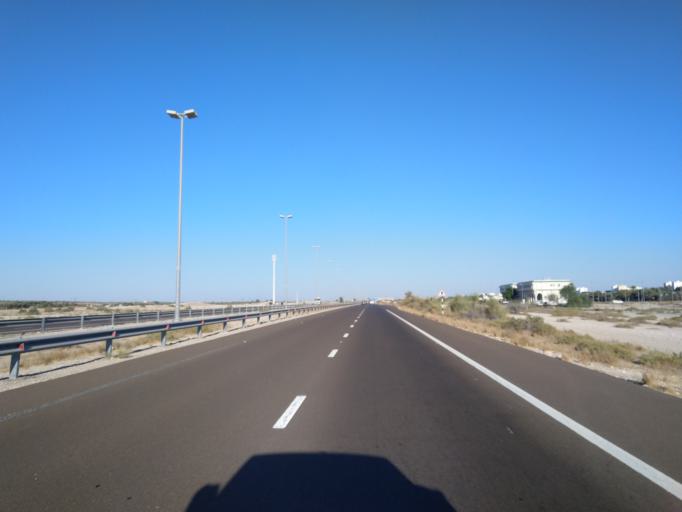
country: OM
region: Al Buraimi
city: Al Buraymi
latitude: 24.5223
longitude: 55.5344
